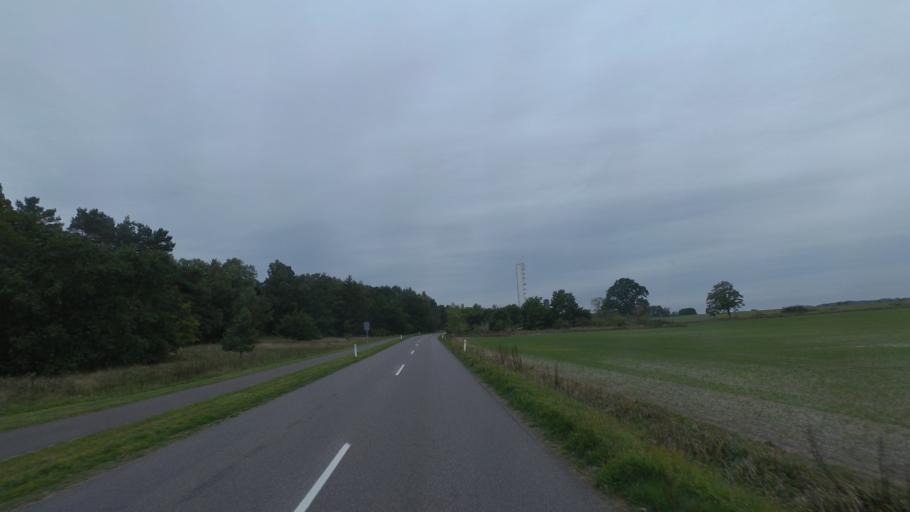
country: DK
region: Capital Region
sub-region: Bornholm Kommune
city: Nexo
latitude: 55.0030
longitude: 15.0808
